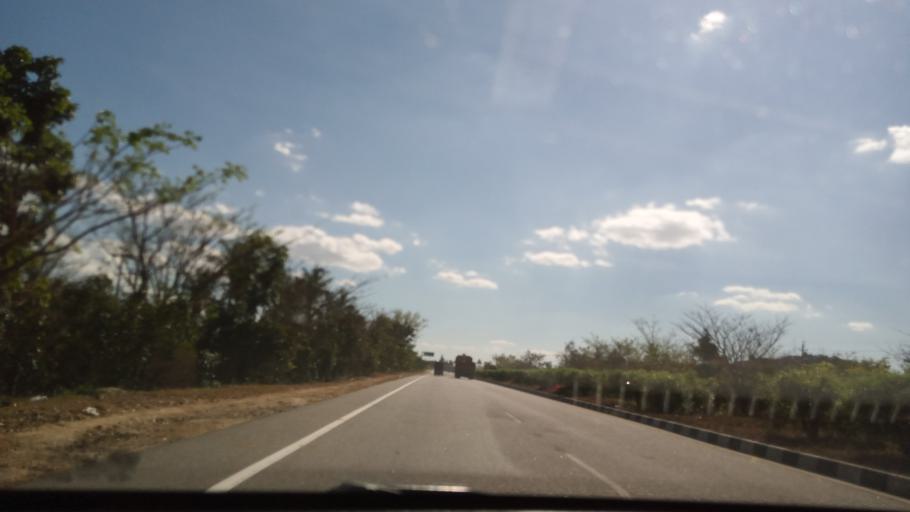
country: IN
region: Karnataka
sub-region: Kolar
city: Mulbagal
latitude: 13.1815
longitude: 78.4181
